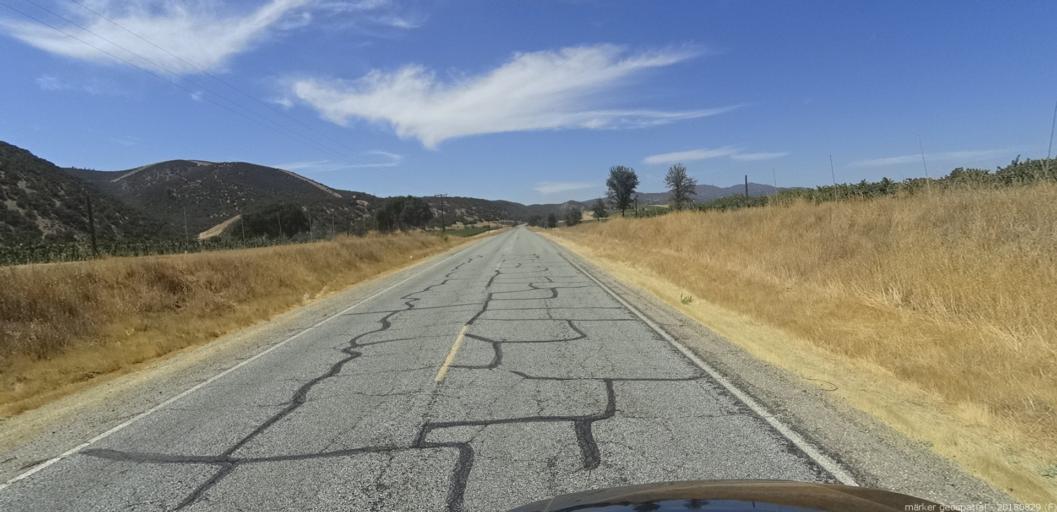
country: US
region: California
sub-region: San Luis Obispo County
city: Lake Nacimiento
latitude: 35.8849
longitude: -120.9140
